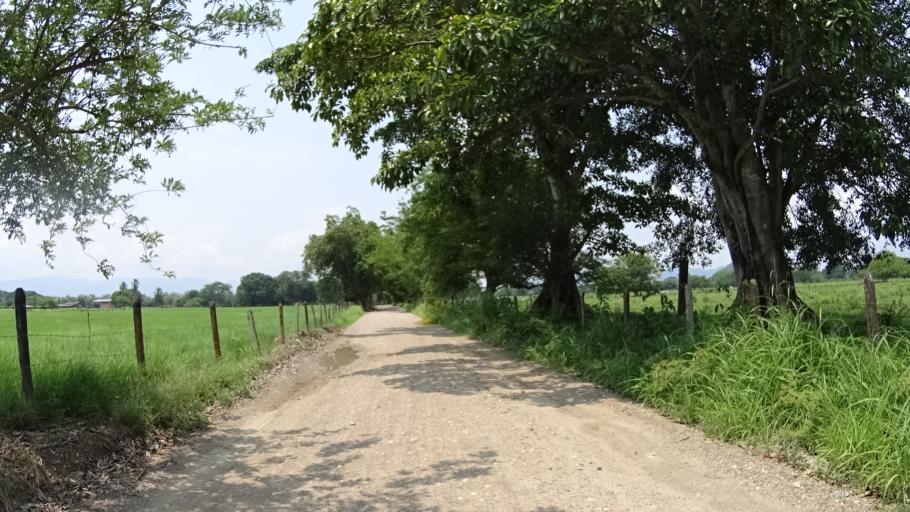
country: CO
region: Cundinamarca
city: Puerto Salgar
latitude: 5.5209
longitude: -74.6880
